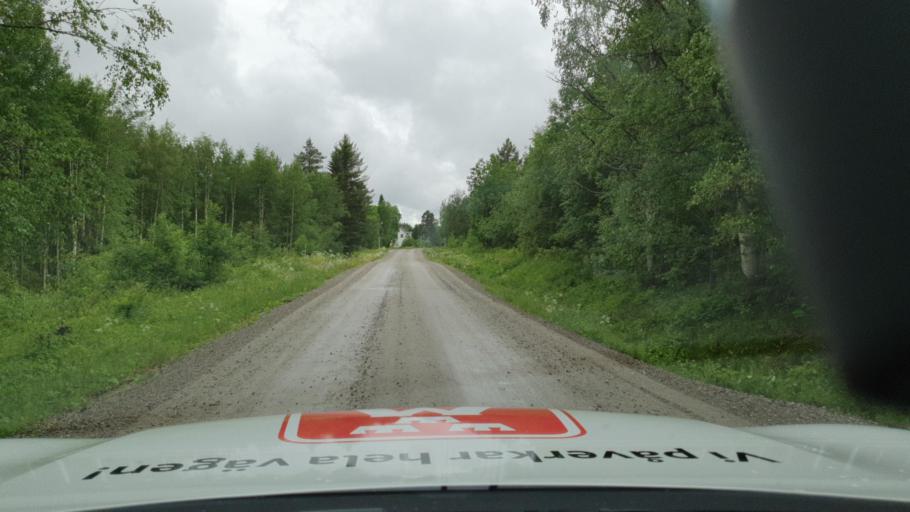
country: SE
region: Vaesterbotten
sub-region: Dorotea Kommun
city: Dorotea
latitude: 64.0155
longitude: 16.7955
